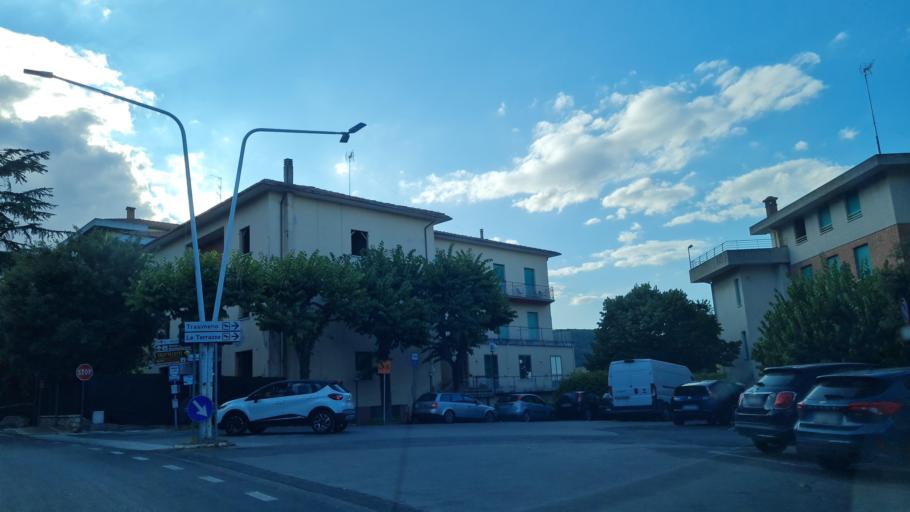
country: IT
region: Tuscany
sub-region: Provincia di Siena
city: Chianciano Terme
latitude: 43.0370
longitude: 11.8243
